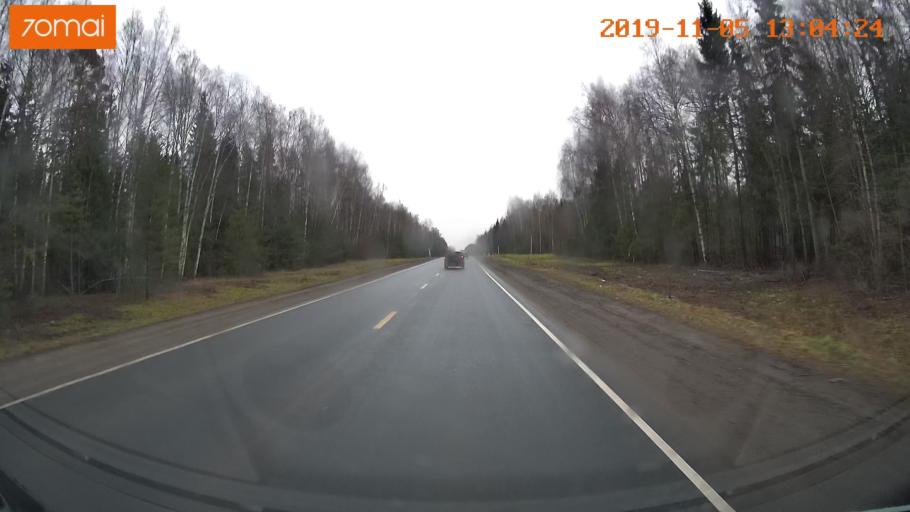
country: RU
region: Ivanovo
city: Kitovo
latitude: 56.8893
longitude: 41.2204
